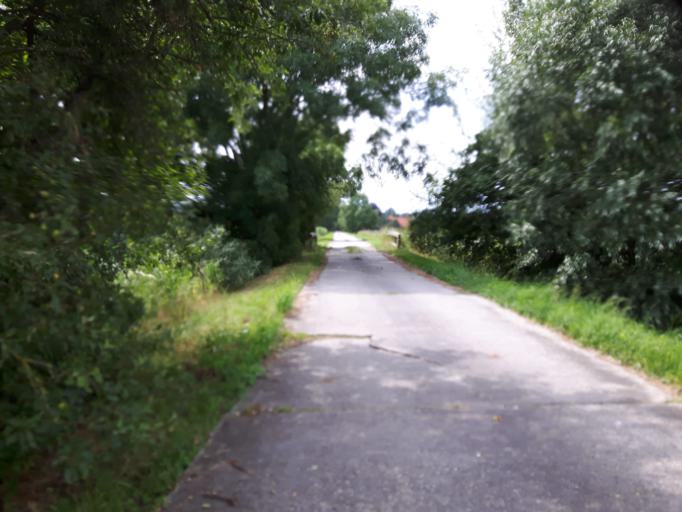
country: DE
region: Lower Saxony
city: Varel
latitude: 53.3891
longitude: 8.2094
